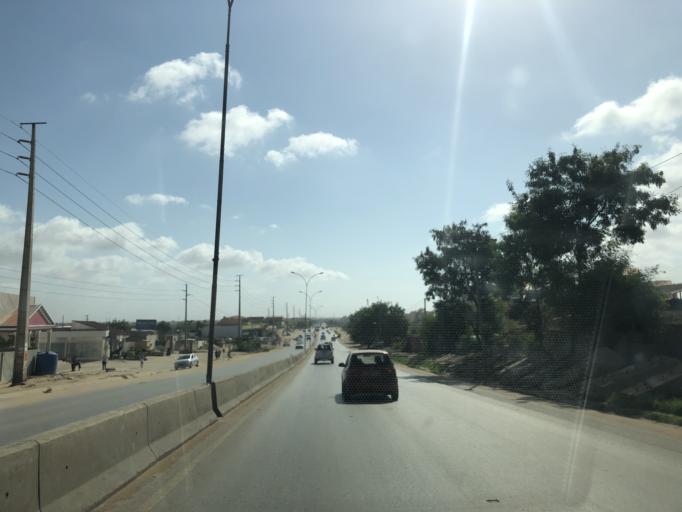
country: AO
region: Luanda
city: Luanda
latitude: -8.9091
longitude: 13.2400
